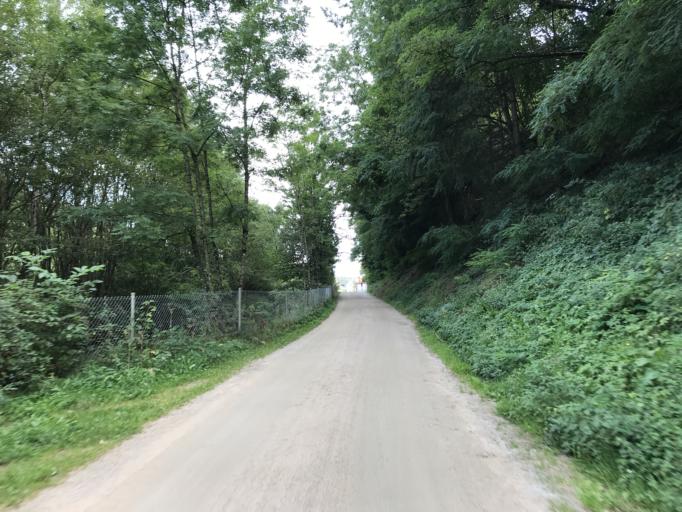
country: DE
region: Baden-Wuerttemberg
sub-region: Freiburg Region
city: Hausen
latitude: 47.6888
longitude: 7.8423
